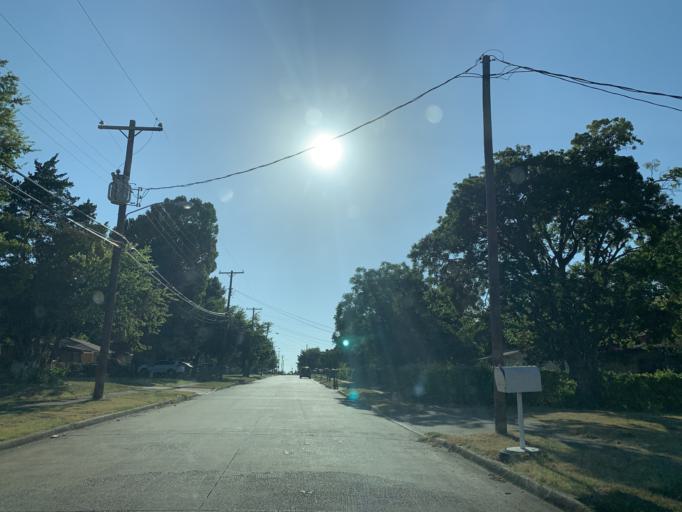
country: US
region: Texas
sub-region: Dallas County
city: Cockrell Hill
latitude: 32.7120
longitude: -96.9047
